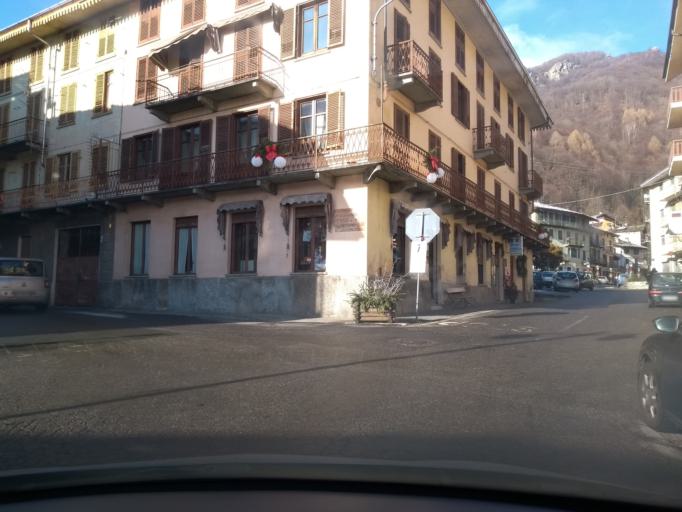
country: IT
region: Piedmont
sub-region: Provincia di Torino
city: Ceres
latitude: 45.3132
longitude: 7.3889
